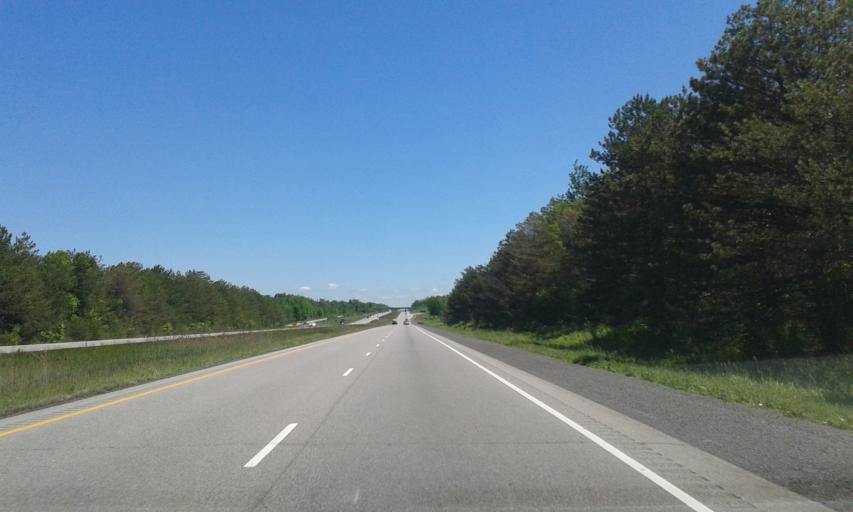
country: US
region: New York
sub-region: St. Lawrence County
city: Ogdensburg
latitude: 44.8030
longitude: -75.4174
